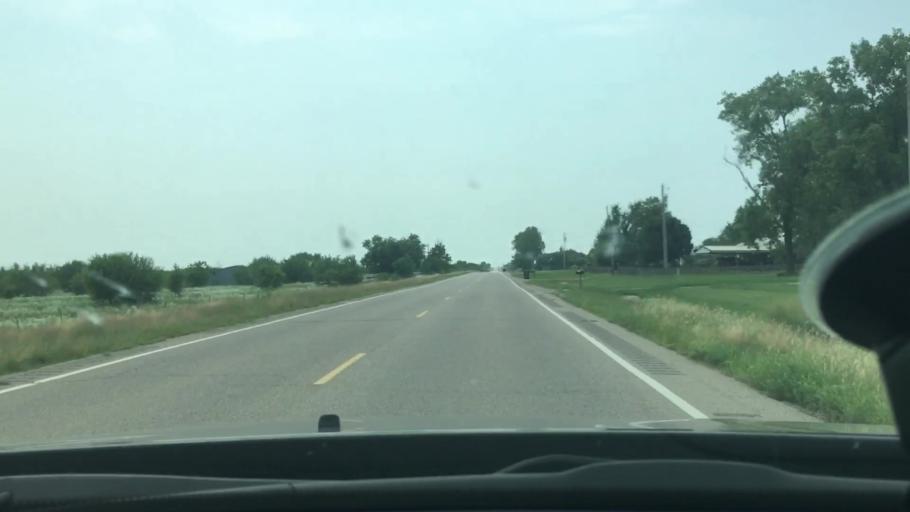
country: US
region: Oklahoma
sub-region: Marshall County
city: Madill
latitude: 34.0492
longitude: -96.7611
